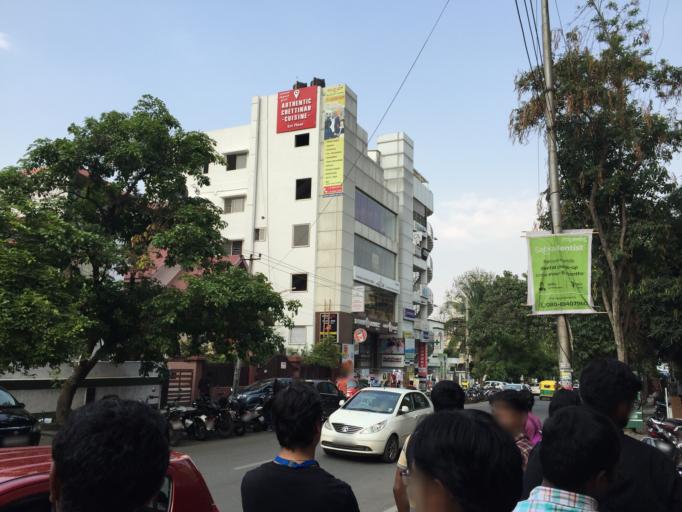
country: IN
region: Karnataka
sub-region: Bangalore Urban
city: Bangalore
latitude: 13.0216
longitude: 77.6405
